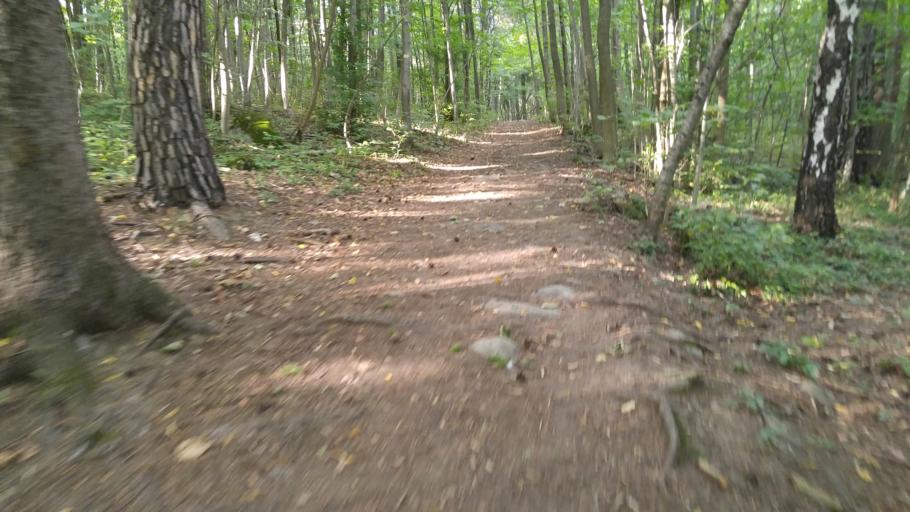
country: NO
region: Akershus
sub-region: Asker
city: Billingstad
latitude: 59.8441
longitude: 10.4884
